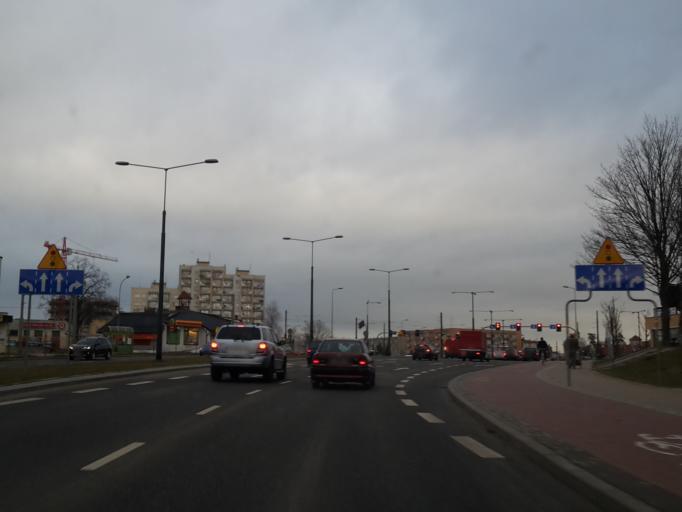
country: PL
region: Warmian-Masurian Voivodeship
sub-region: Powiat elblaski
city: Elblag
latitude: 54.1647
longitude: 19.4056
